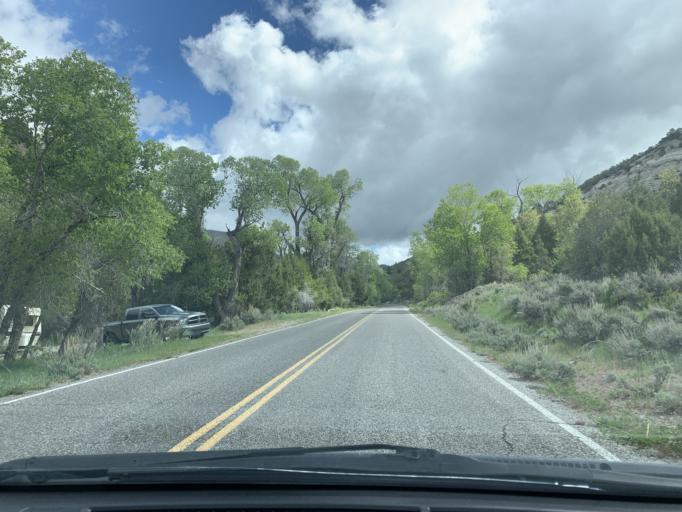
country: US
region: Utah
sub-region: Juab County
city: Nephi
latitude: 39.7644
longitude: -111.7084
